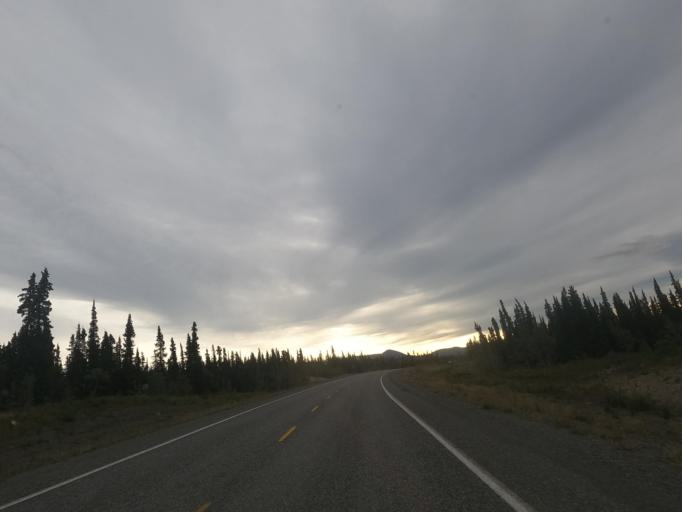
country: CA
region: Yukon
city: Haines Junction
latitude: 60.8126
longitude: -136.4964
